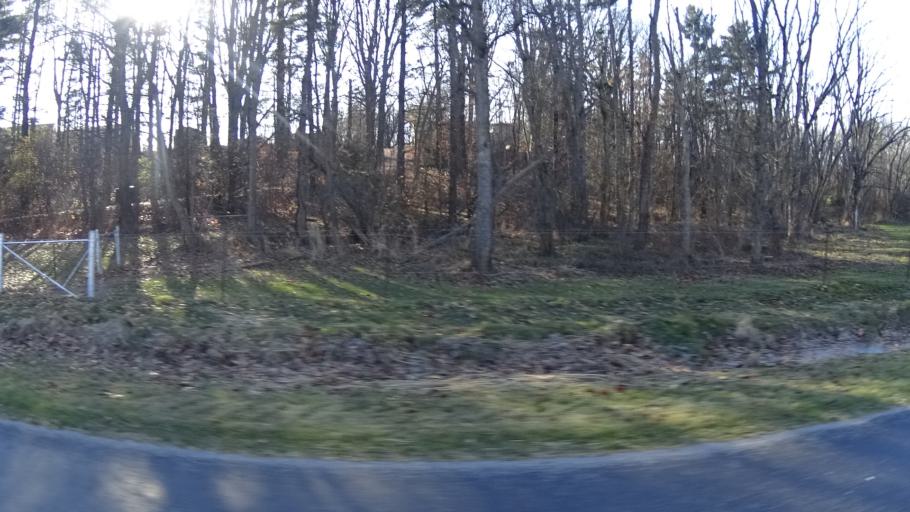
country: US
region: Ohio
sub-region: Lorain County
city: Oberlin
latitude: 41.2513
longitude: -82.1859
